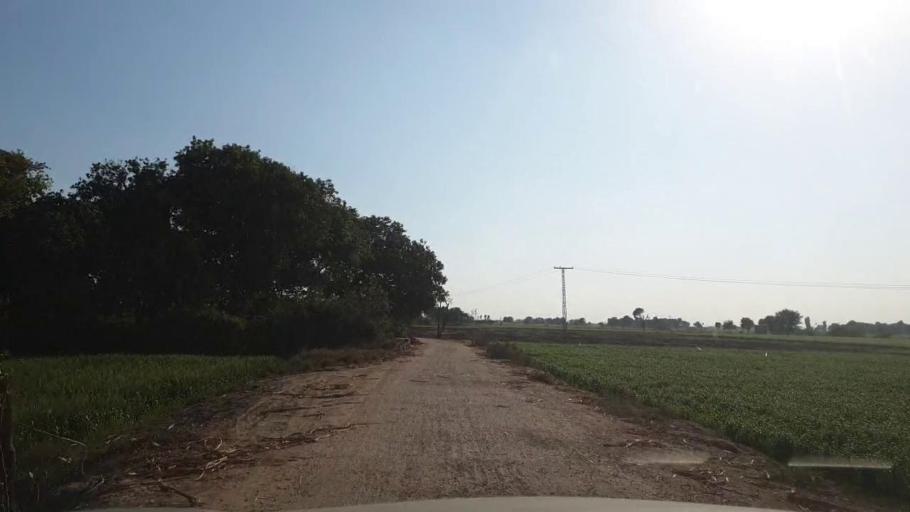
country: PK
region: Sindh
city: Tando Adam
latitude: 25.6867
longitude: 68.6883
